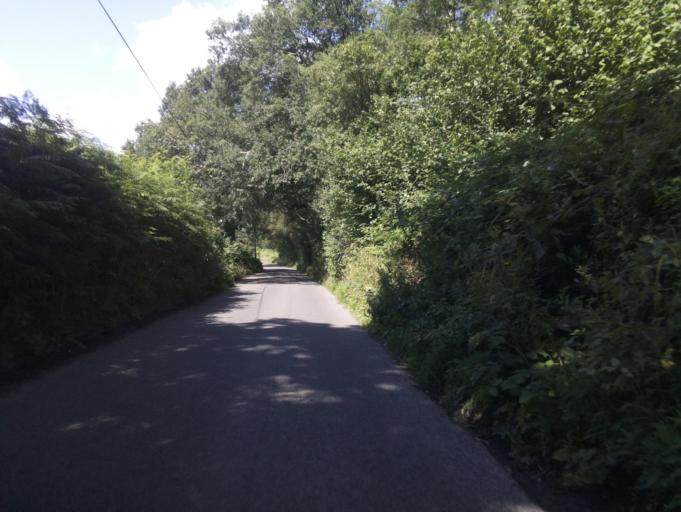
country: GB
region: England
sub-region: West Berkshire
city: Greenham
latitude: 51.3525
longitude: -1.2818
